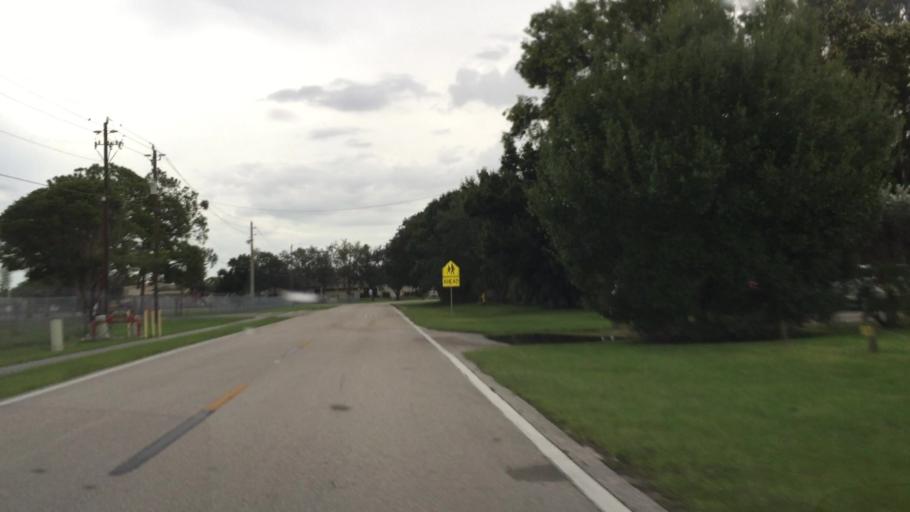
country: US
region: Florida
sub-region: Lee County
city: Pine Manor
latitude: 26.5677
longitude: -81.8695
